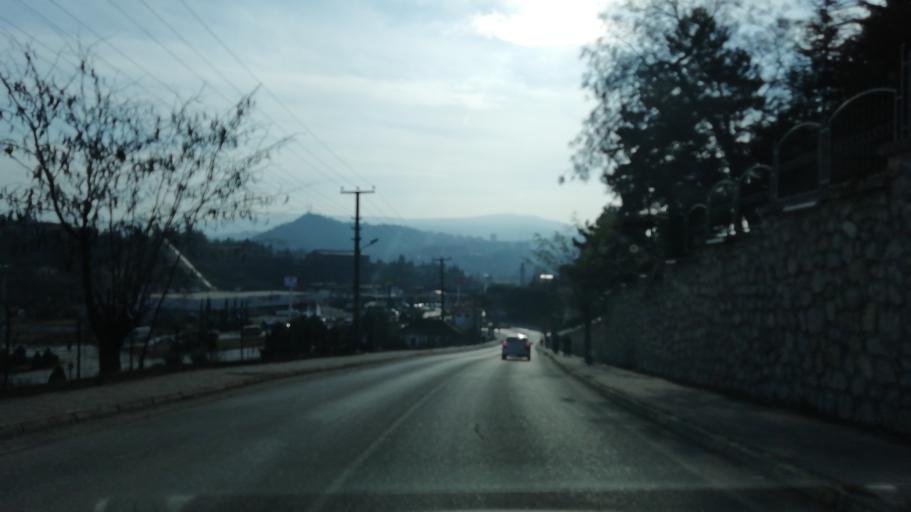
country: TR
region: Karabuk
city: Karabuk
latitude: 41.2000
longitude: 32.6267
